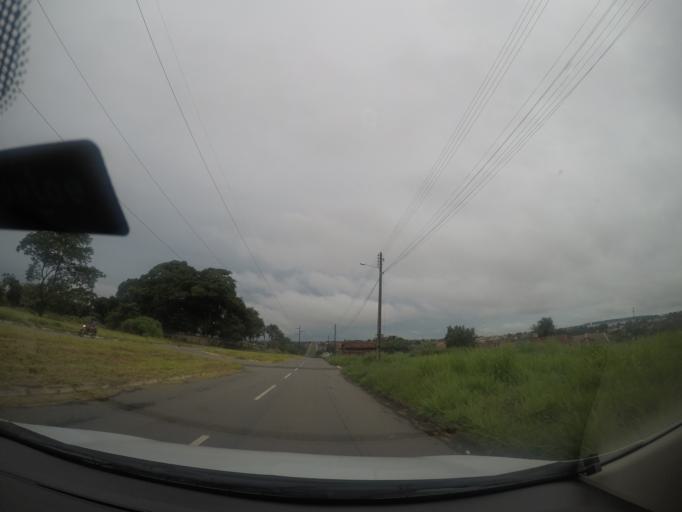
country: BR
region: Goias
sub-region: Aparecida De Goiania
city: Aparecida de Goiania
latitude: -16.7627
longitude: -49.3064
